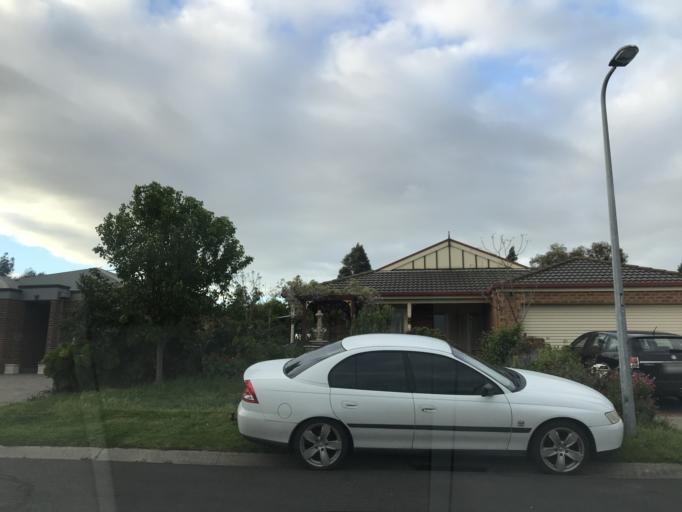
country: AU
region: Victoria
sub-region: Brimbank
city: Sunshine West
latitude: -37.7968
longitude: 144.8024
